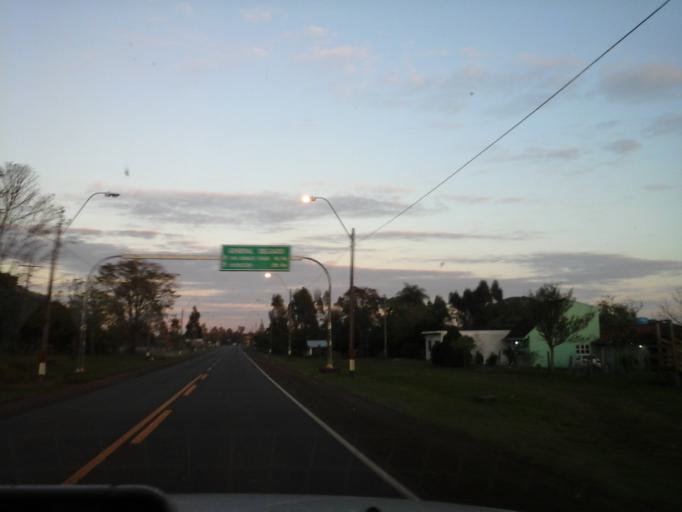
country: PY
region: Itapua
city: General Delgado
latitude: -27.0899
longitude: -56.5148
